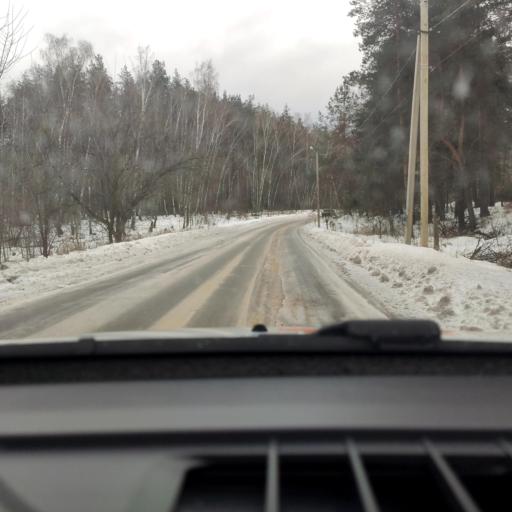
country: RU
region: Voronezj
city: Podgornoye
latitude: 51.7516
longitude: 39.1561
